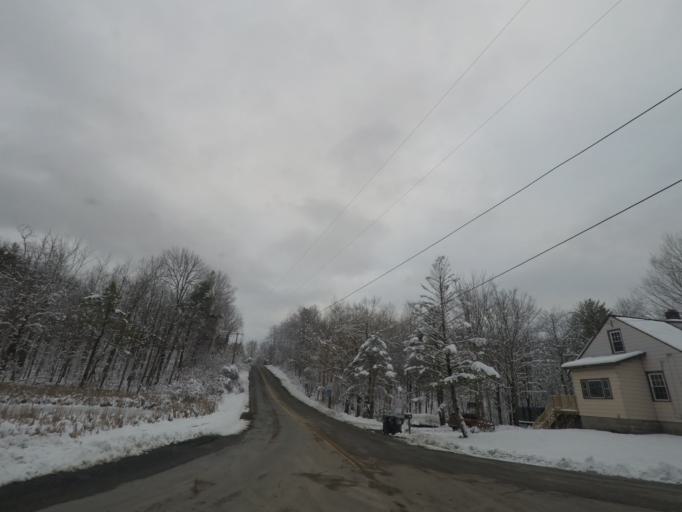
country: US
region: New York
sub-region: Rensselaer County
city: Averill Park
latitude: 42.6664
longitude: -73.5186
